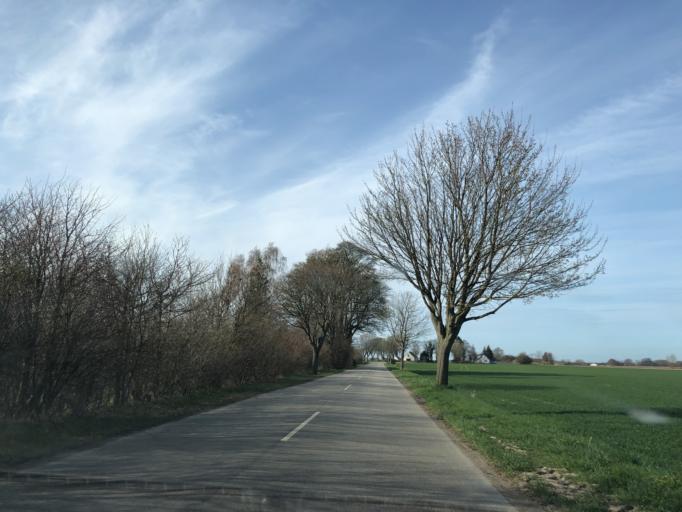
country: DK
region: Zealand
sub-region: Stevns Kommune
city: Store Heddinge
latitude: 55.3125
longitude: 12.4357
